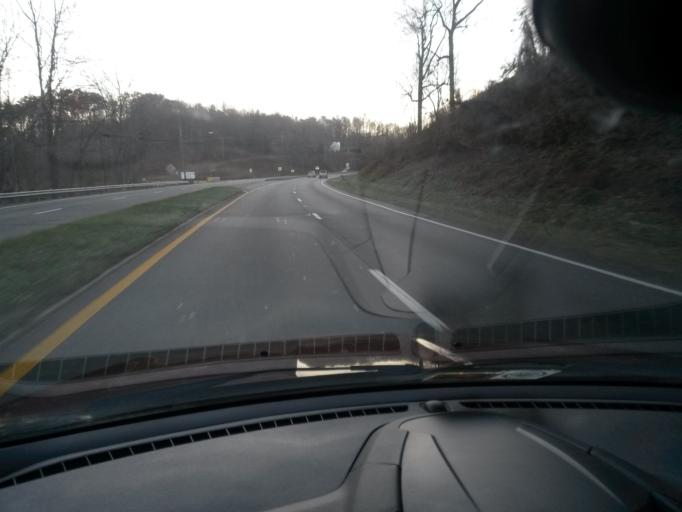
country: US
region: Virginia
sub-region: Roanoke County
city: Narrows
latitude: 37.1122
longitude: -79.9492
